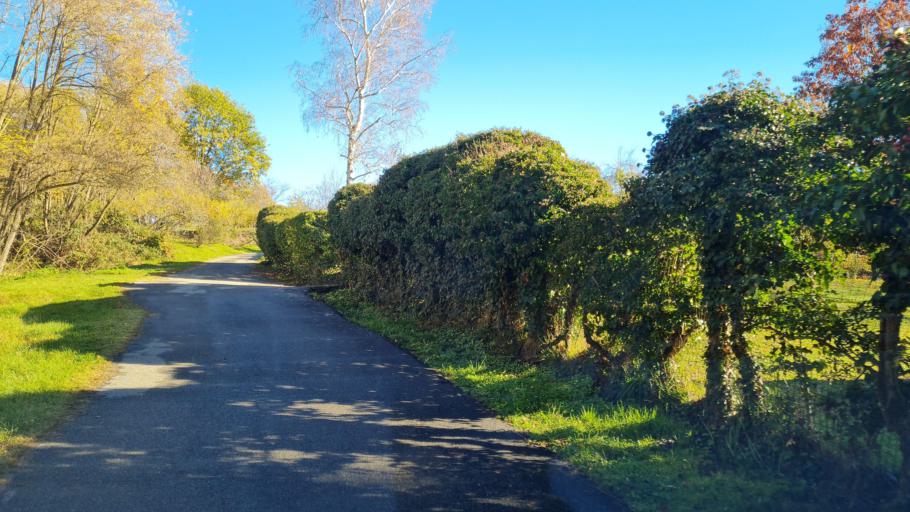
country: IT
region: Piedmont
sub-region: Provincia di Biella
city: Brusnengo
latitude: 45.5956
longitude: 8.2603
